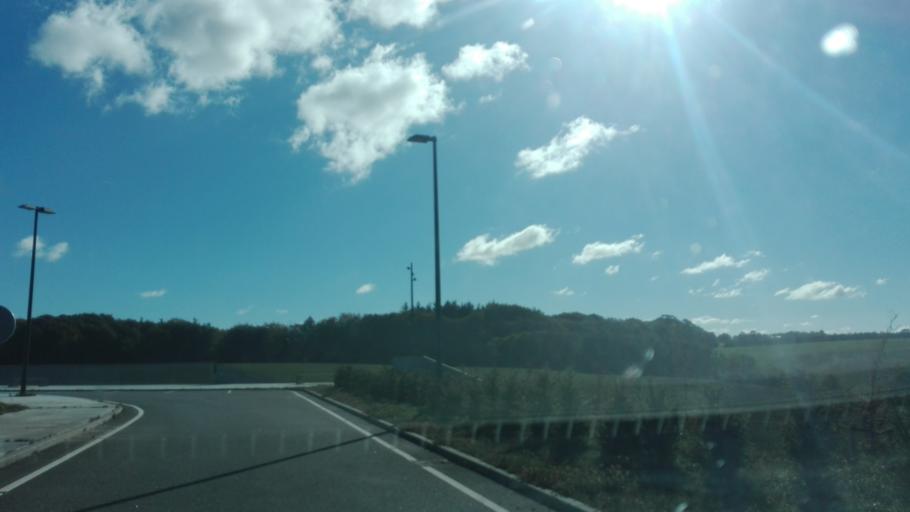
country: DK
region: Central Jutland
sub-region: Skanderborg Kommune
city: Ry
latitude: 56.1481
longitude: 9.7596
